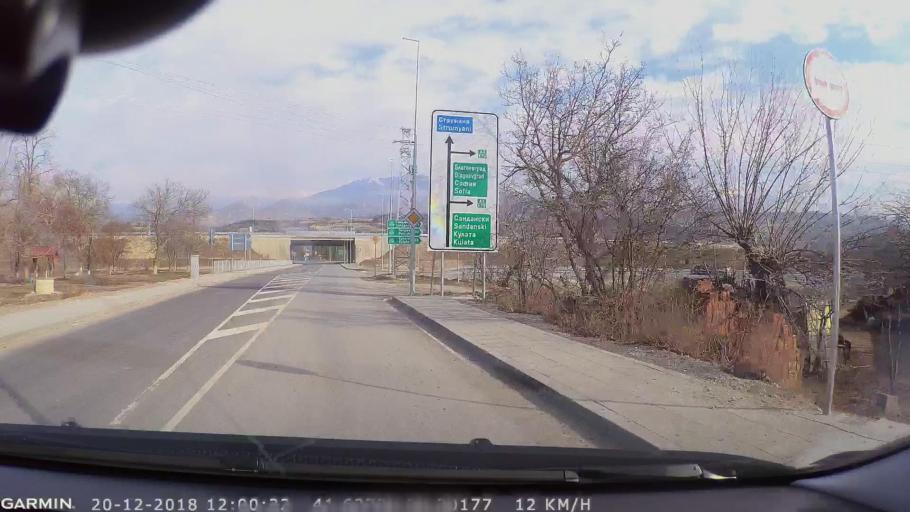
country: BG
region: Blagoevgrad
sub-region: Obshtina Strumyani
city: Strumyani
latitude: 41.6274
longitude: 23.2017
